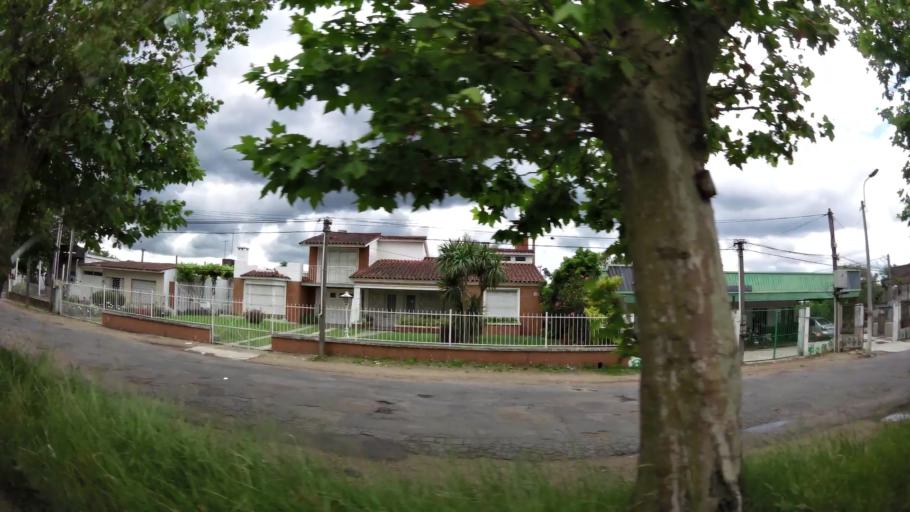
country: UY
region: Canelones
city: Toledo
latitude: -34.8048
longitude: -56.1366
